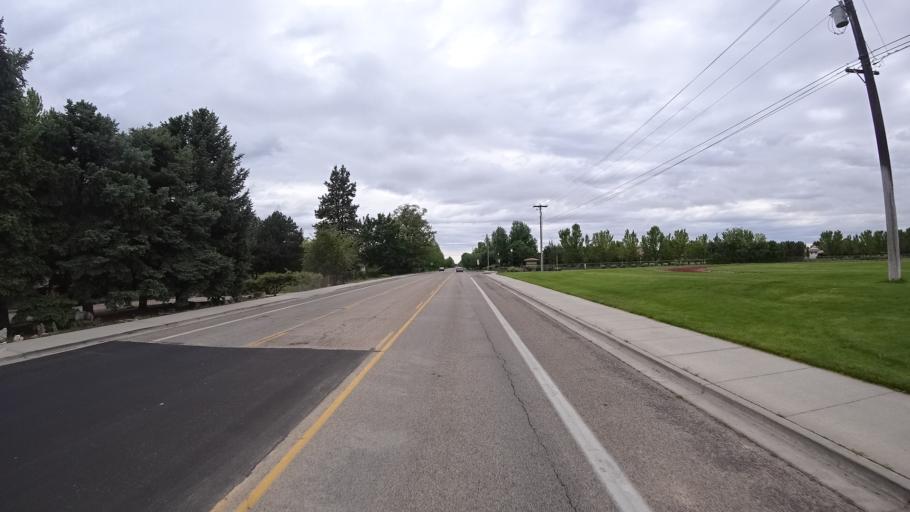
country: US
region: Idaho
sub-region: Ada County
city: Eagle
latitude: 43.7065
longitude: -116.3677
